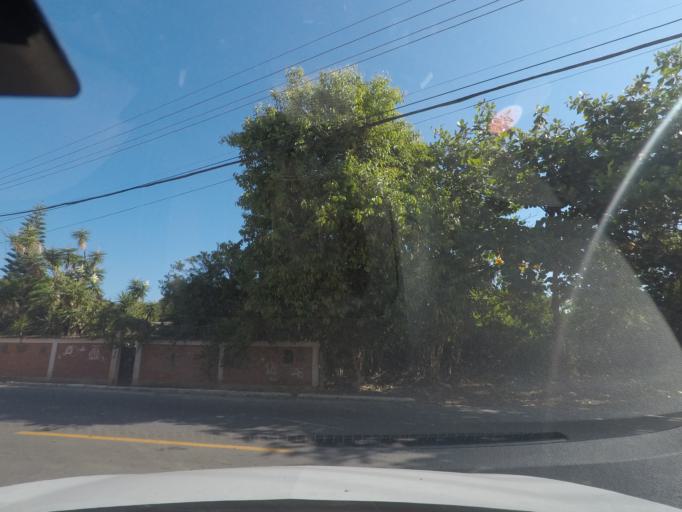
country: BR
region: Rio de Janeiro
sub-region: Marica
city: Marica
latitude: -22.9714
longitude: -42.9244
